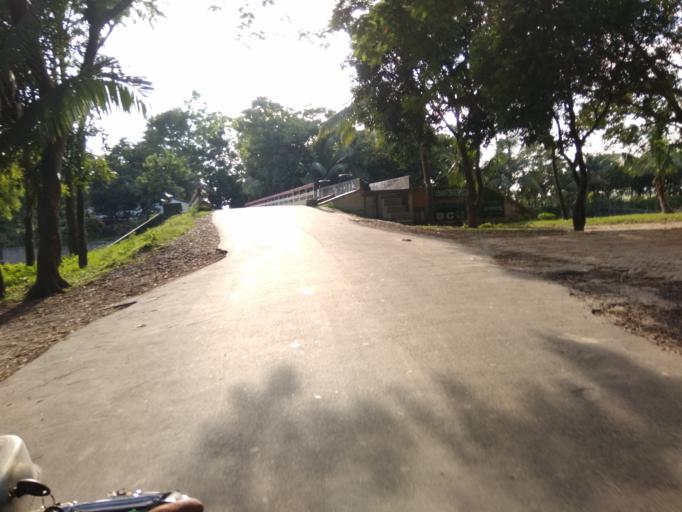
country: BD
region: Rangpur Division
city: Rangpur
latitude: 25.8324
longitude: 89.1136
